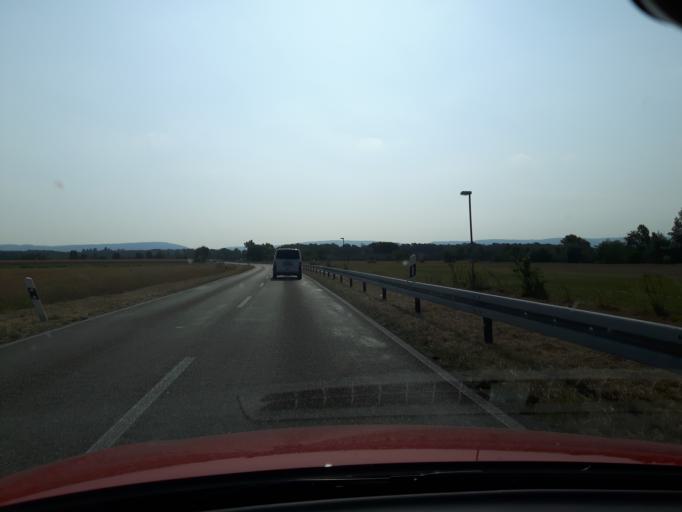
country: DE
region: Baden-Wuerttemberg
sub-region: Karlsruhe Region
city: Rheinstetten
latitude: 48.9703
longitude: 8.3242
